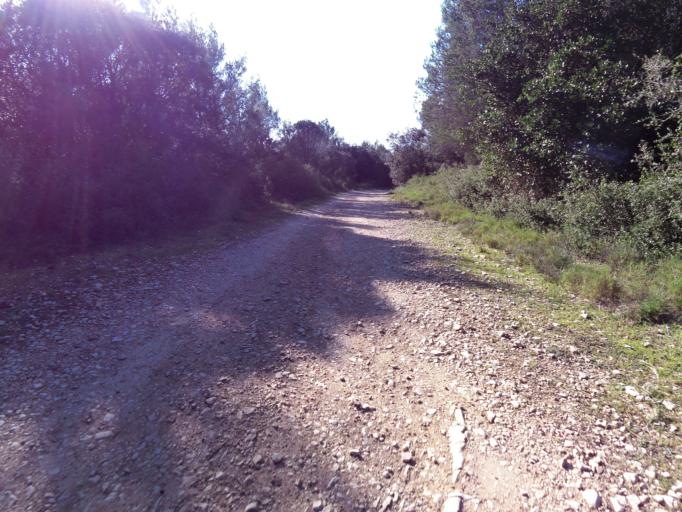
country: FR
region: Languedoc-Roussillon
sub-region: Departement du Gard
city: Congenies
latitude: 43.7613
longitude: 4.1672
